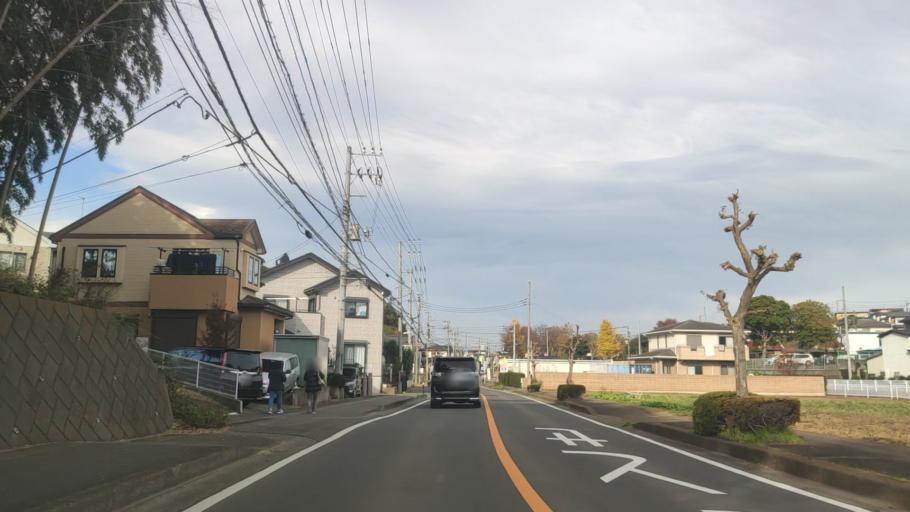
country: JP
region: Kanagawa
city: Atsugi
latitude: 35.4313
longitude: 139.4045
